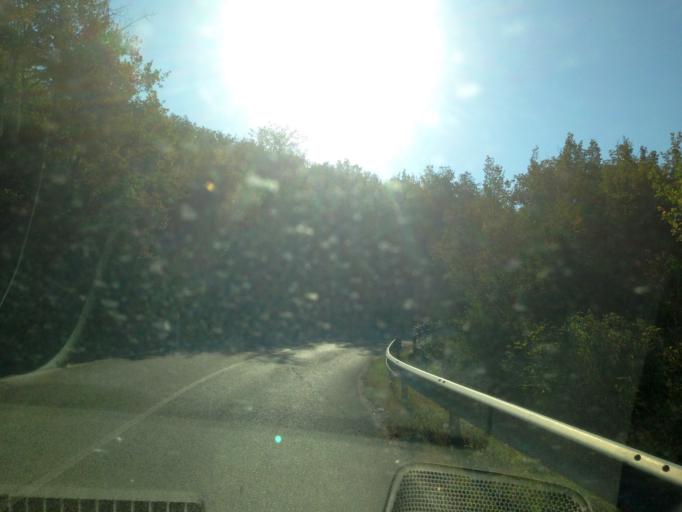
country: IT
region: Tuscany
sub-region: Provincia di Siena
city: Castellina in Chianti
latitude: 43.5070
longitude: 11.2921
